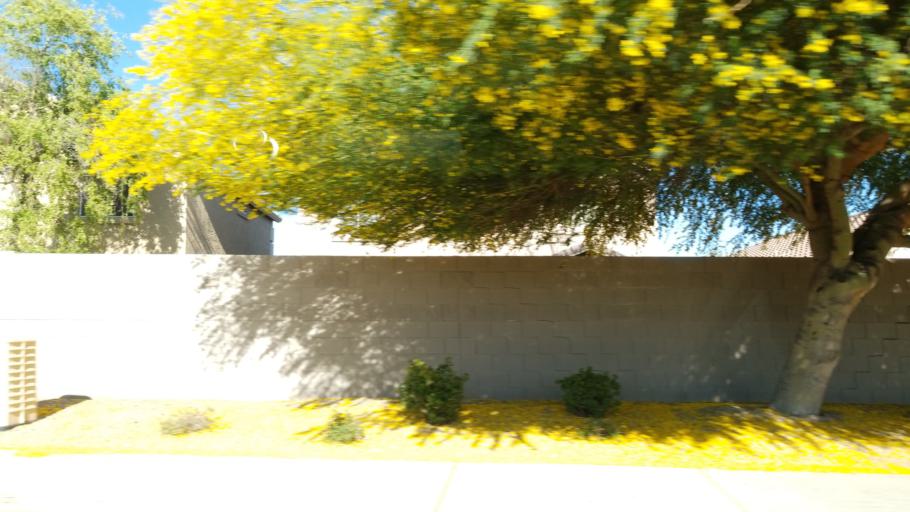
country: US
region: Arizona
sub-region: Maricopa County
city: Youngtown
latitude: 33.5736
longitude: -112.3112
